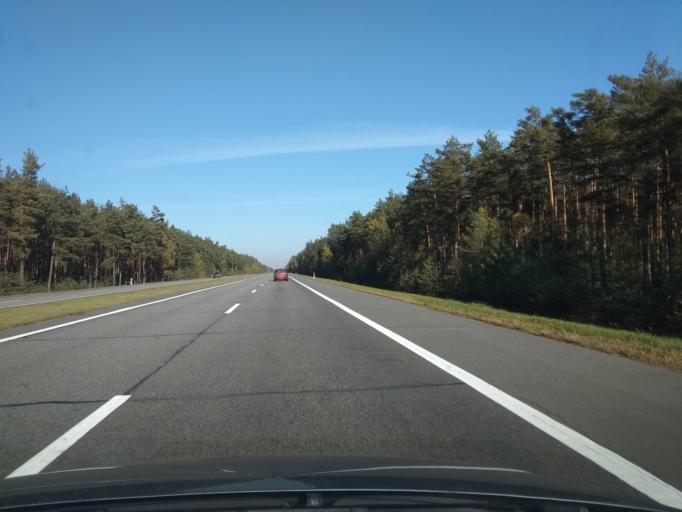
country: BY
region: Grodnenskaya
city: Zhyrovichy
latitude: 52.9335
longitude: 25.6998
